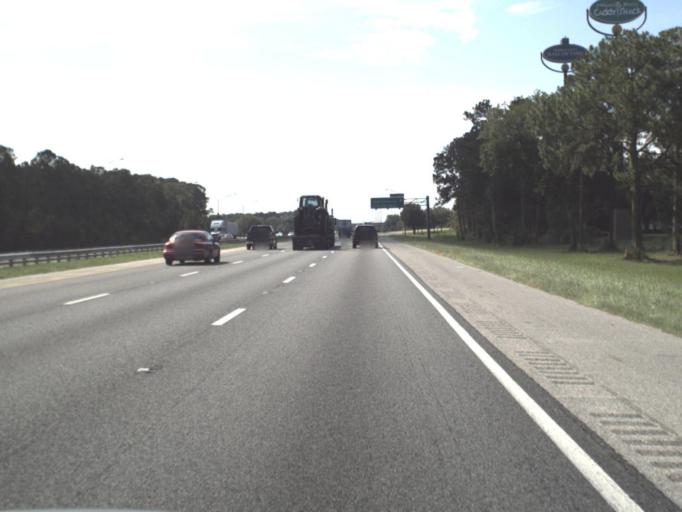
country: US
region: Florida
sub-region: Saint Johns County
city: Villano Beach
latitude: 29.9939
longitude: -81.4667
